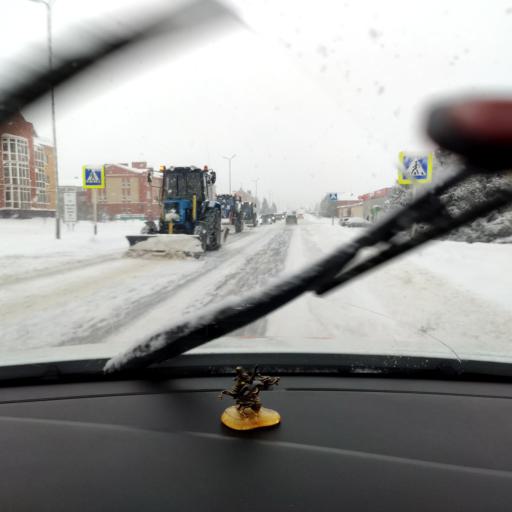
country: RU
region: Tatarstan
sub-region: Arskiy Rayon
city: Arsk
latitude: 56.0994
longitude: 49.8756
